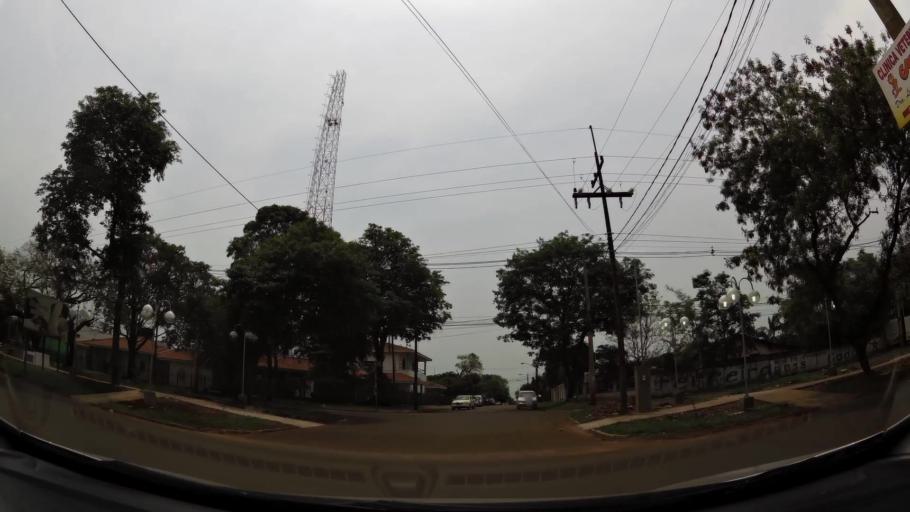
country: PY
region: Alto Parana
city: Presidente Franco
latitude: -25.5554
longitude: -54.6273
